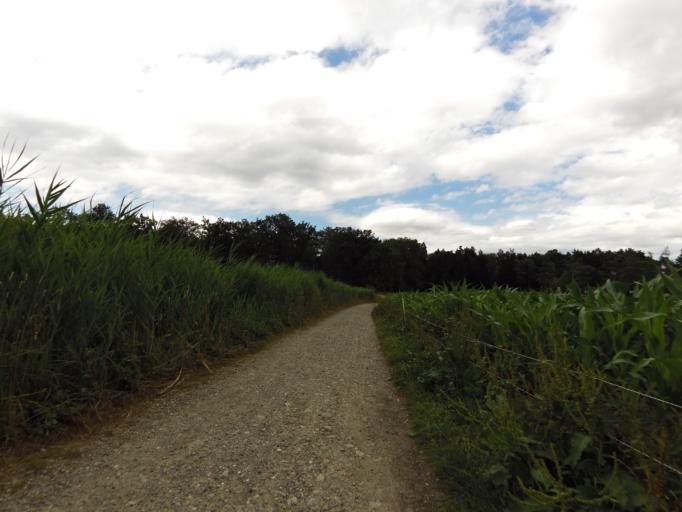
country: CH
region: Zurich
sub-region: Bezirk Zuerich
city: Zuerich (Kreis 10)
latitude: 47.4076
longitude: 8.5021
